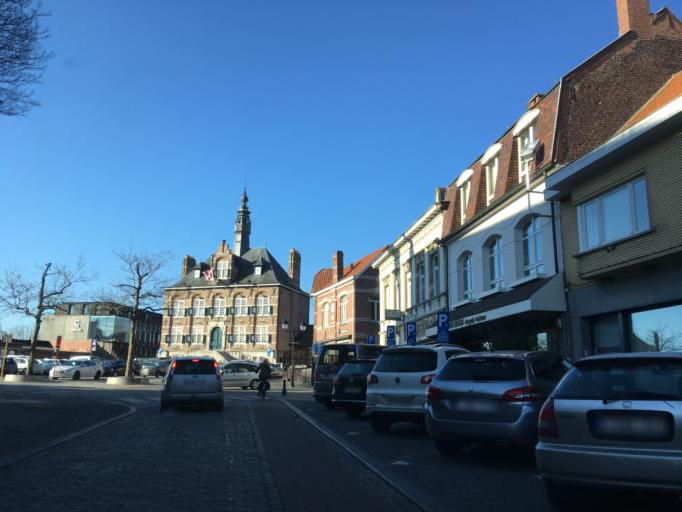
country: BE
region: Flanders
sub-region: Provincie Oost-Vlaanderen
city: Zomergem
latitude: 51.1187
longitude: 3.5603
